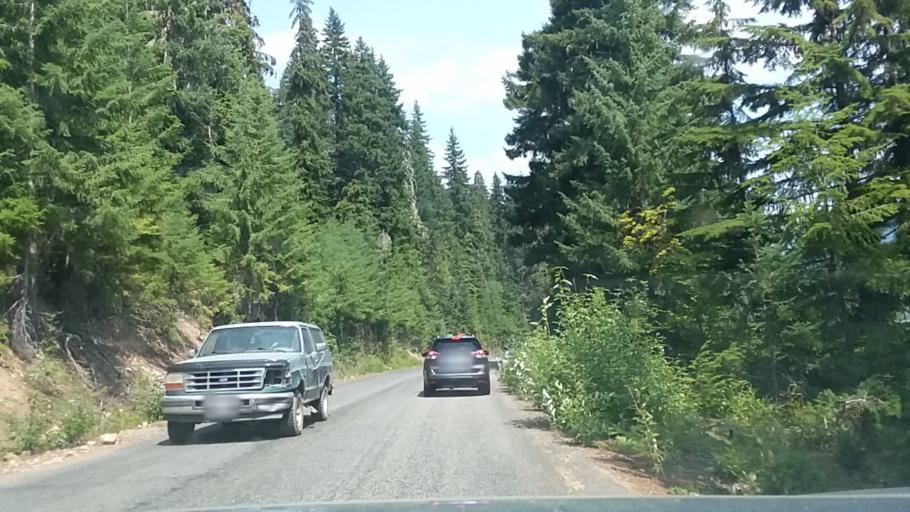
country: US
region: Washington
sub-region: Kittitas County
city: Cle Elum
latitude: 47.3402
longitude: -121.2539
